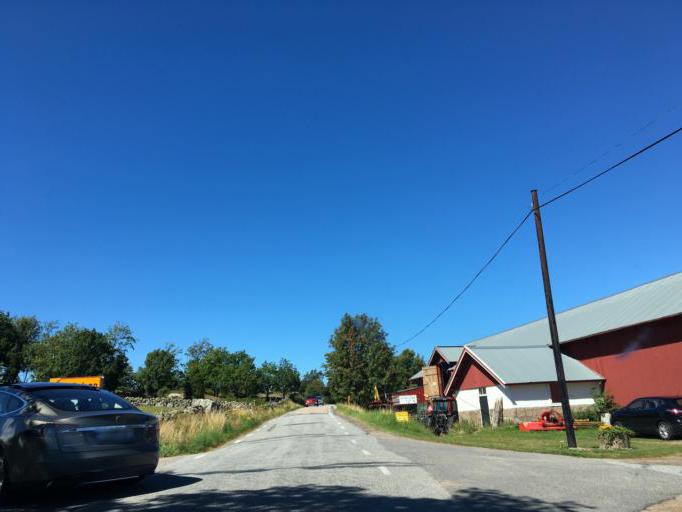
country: SE
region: Vaestra Goetaland
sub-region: Sotenas Kommun
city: Hunnebostrand
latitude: 58.4279
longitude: 11.2656
